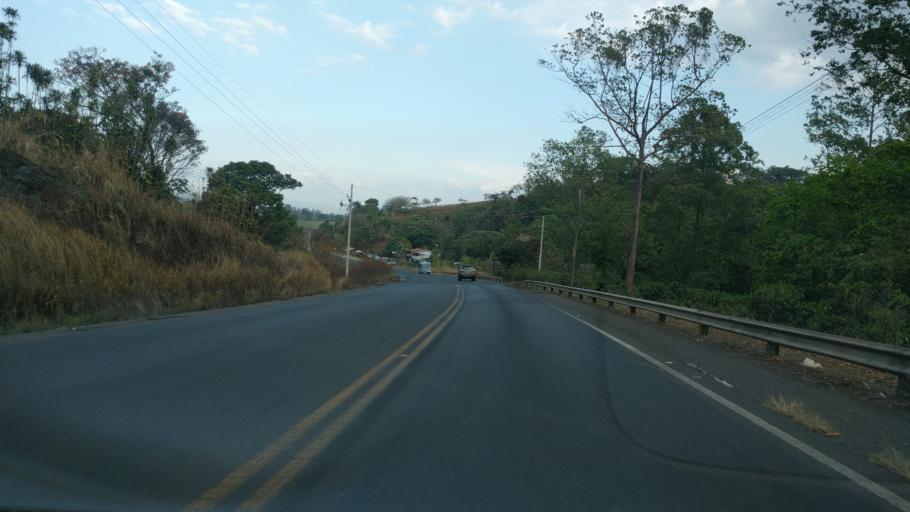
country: CR
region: Alajuela
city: Naranjo
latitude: 10.0671
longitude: -84.3671
